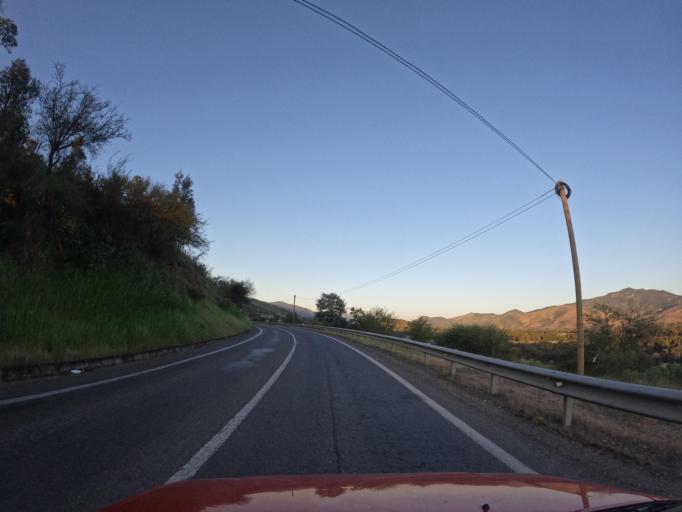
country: CL
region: Maule
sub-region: Provincia de Talca
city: Talca
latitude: -35.0874
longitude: -71.6453
